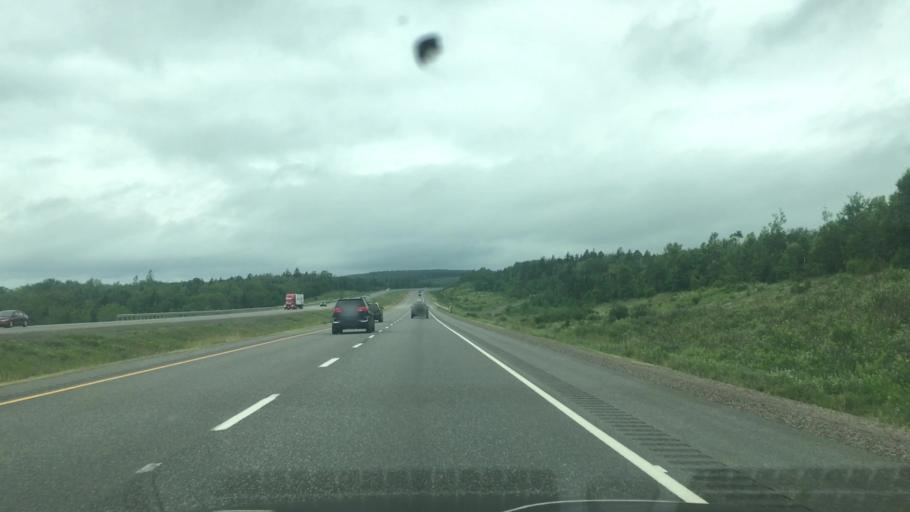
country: CA
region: Nova Scotia
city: Oxford
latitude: 45.4520
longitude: -63.6257
